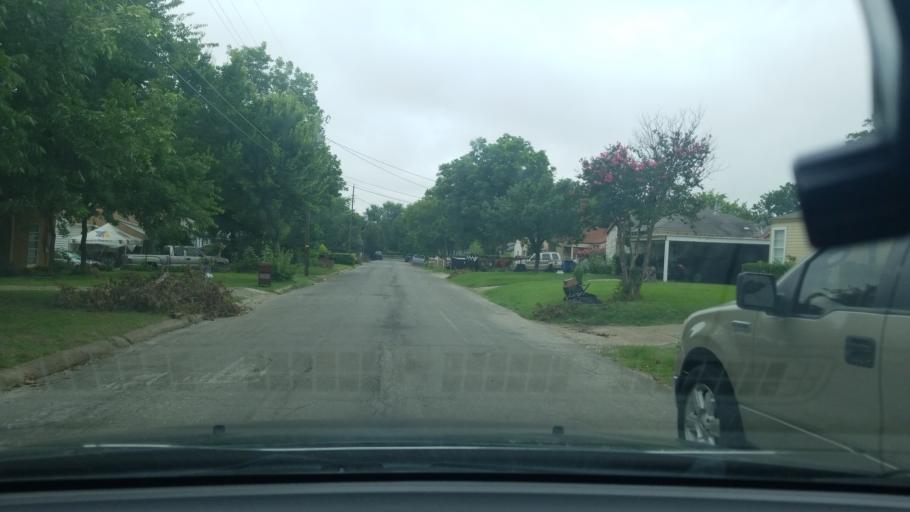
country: US
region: Texas
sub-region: Dallas County
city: Balch Springs
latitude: 32.7674
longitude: -96.6867
